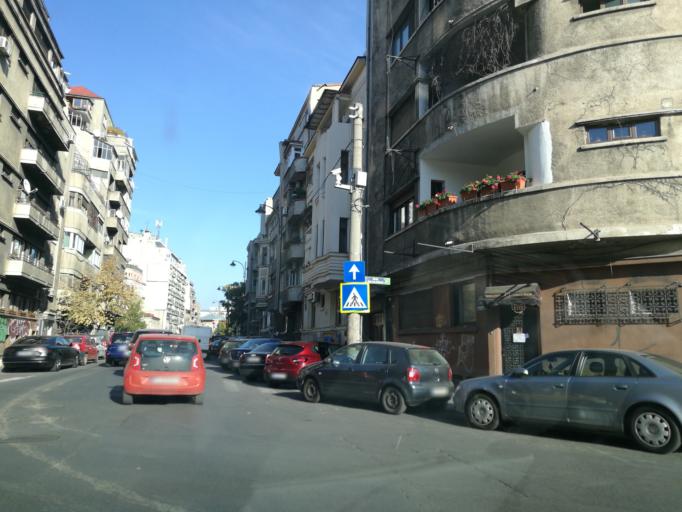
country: RO
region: Bucuresti
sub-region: Municipiul Bucuresti
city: Bucharest
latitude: 44.4413
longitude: 26.1043
